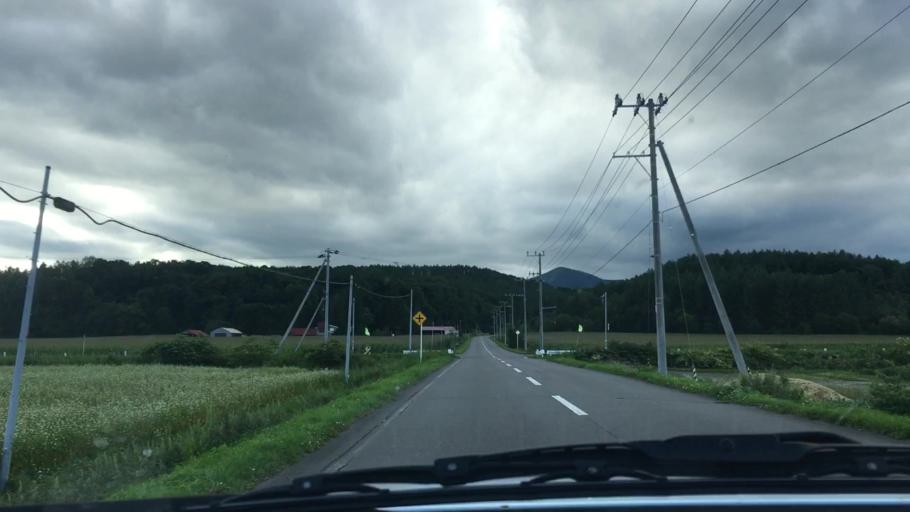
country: JP
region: Hokkaido
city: Otofuke
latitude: 43.1406
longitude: 142.8898
